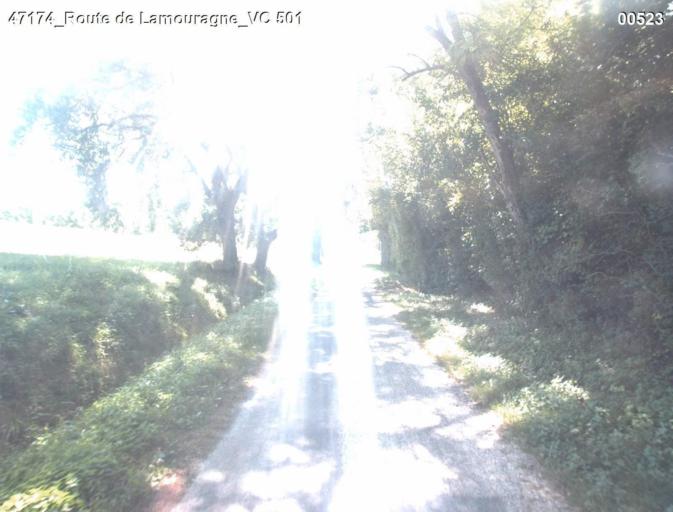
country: FR
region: Midi-Pyrenees
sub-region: Departement du Gers
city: Condom
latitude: 44.0429
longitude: 0.3857
